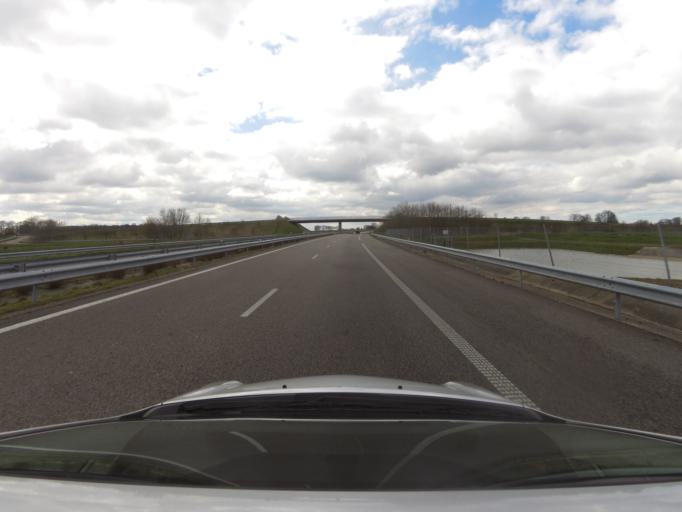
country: FR
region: Haute-Normandie
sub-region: Departement de la Seine-Maritime
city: Lanquetot
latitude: 49.6070
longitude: 0.5058
